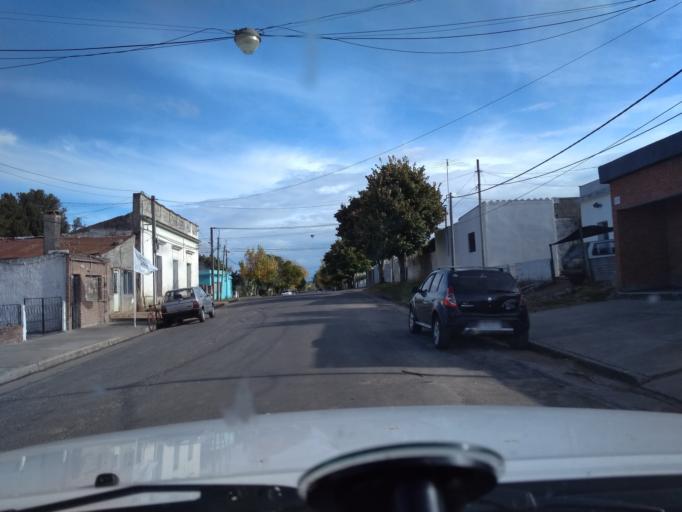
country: UY
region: Florida
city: Florida
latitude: -34.1052
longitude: -56.2194
